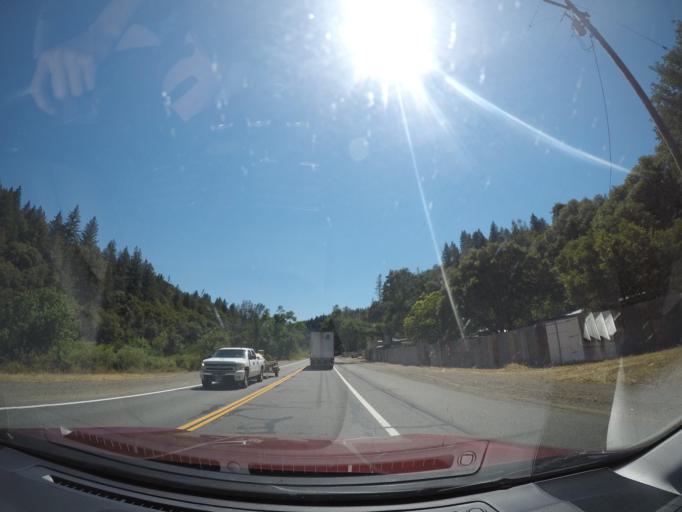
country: US
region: California
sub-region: Shasta County
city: Bella Vista
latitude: 40.7277
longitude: -122.0773
